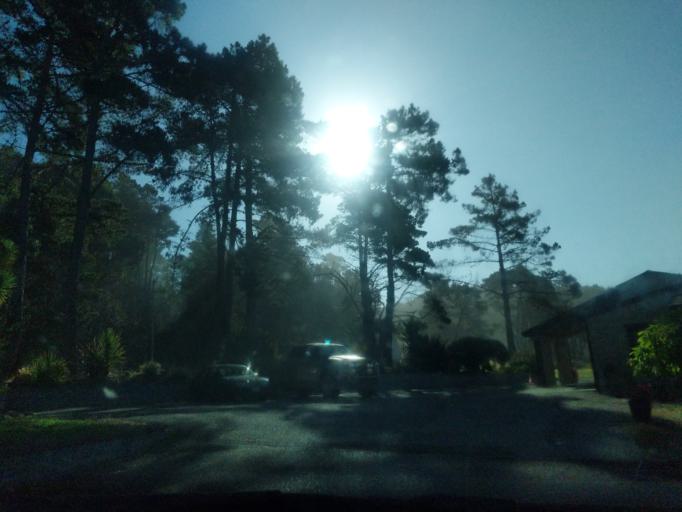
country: US
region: California
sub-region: Sonoma County
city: Monte Rio
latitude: 38.5272
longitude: -123.2639
